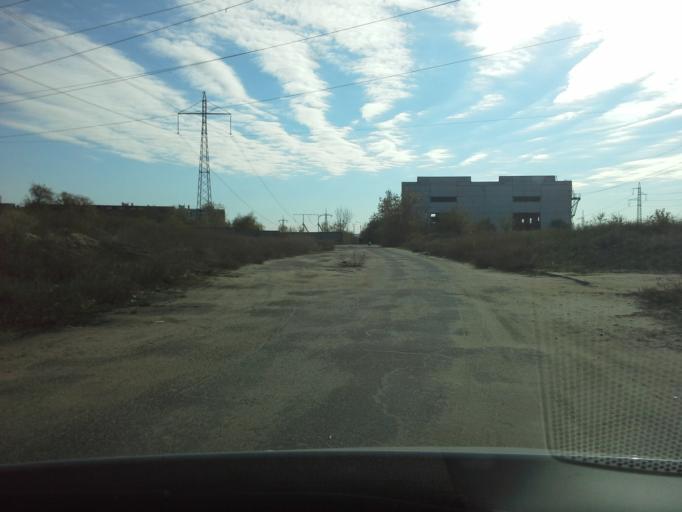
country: RU
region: Volgograd
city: Vodstroy
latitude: 48.8379
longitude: 44.6292
